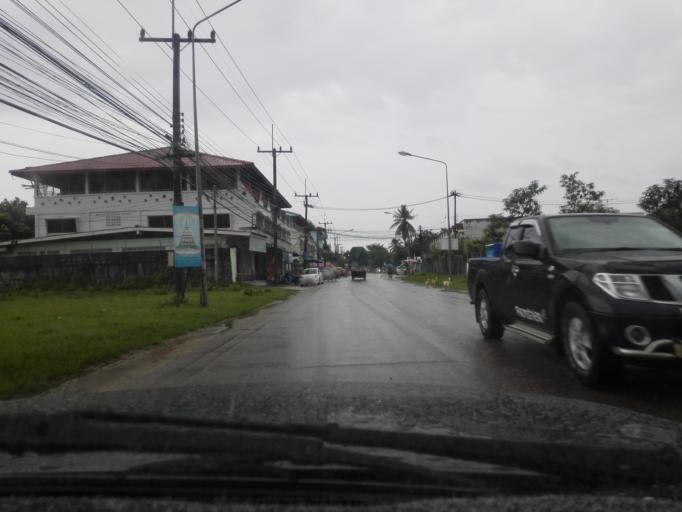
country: TH
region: Tak
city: Mae Sot
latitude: 16.7056
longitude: 98.5717
